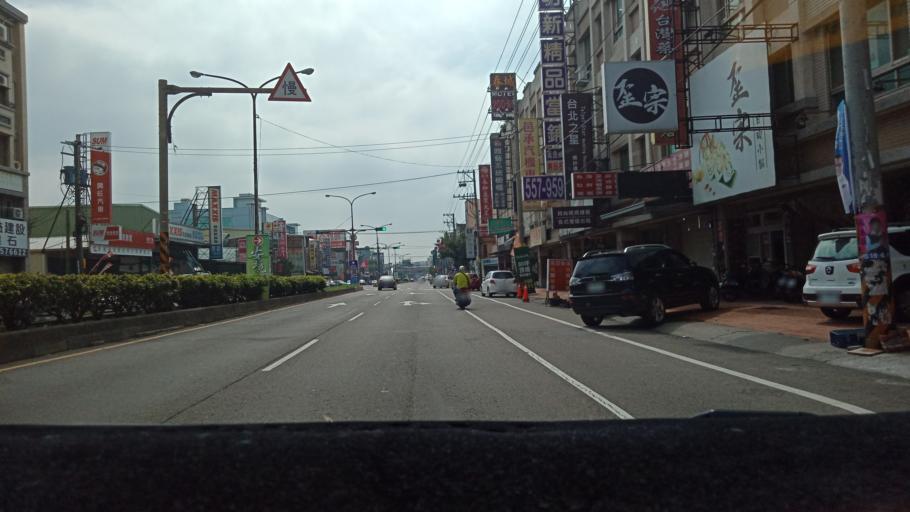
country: TW
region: Taiwan
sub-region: Hsinchu
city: Zhubei
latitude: 24.8738
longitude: 121.0011
